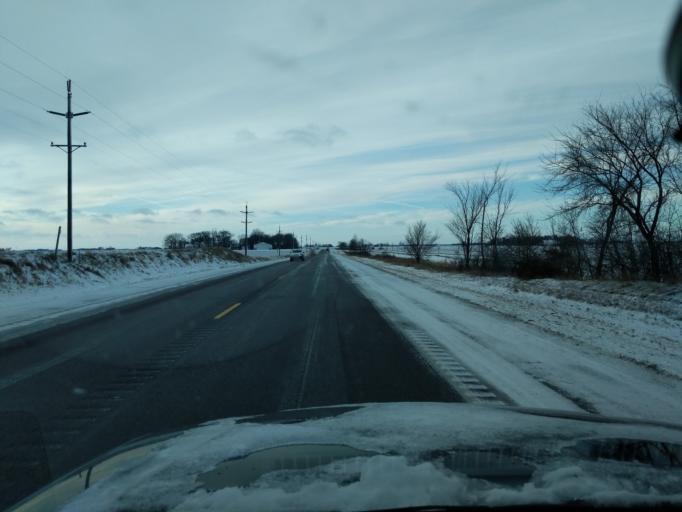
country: US
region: Minnesota
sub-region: Renville County
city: Hector
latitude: 44.7244
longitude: -94.5326
